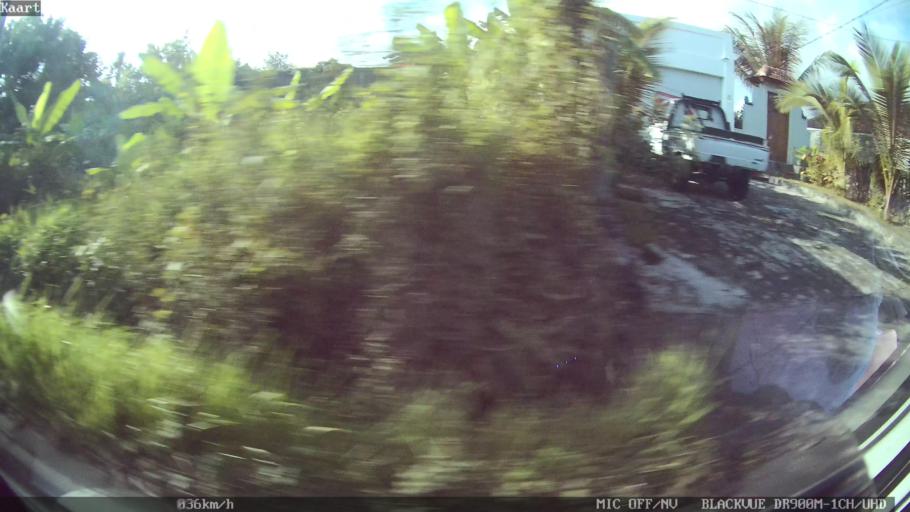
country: ID
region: Bali
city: Banjar Desa
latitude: -8.5797
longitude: 115.2357
